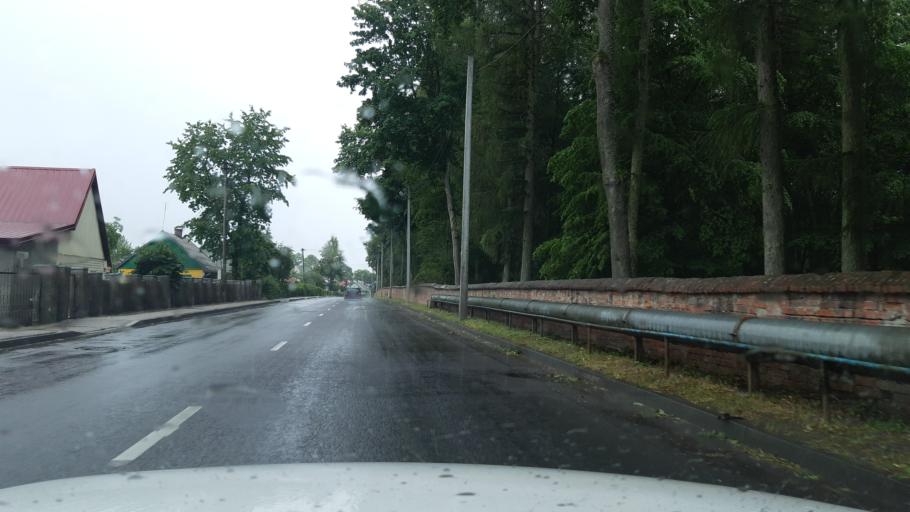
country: LT
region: Taurages apskritis
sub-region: Jurbarkas
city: Jurbarkas
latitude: 55.0817
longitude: 22.7546
